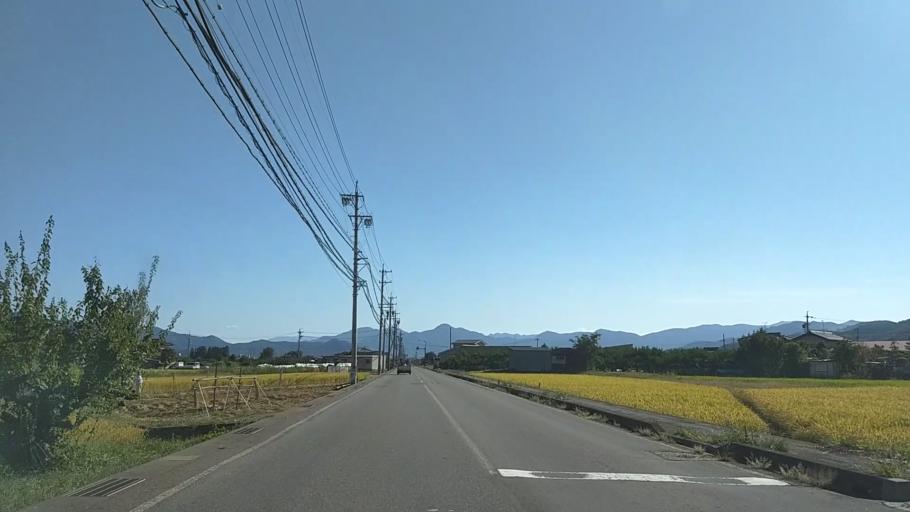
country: JP
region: Nagano
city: Nagano-shi
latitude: 36.6097
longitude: 138.1438
